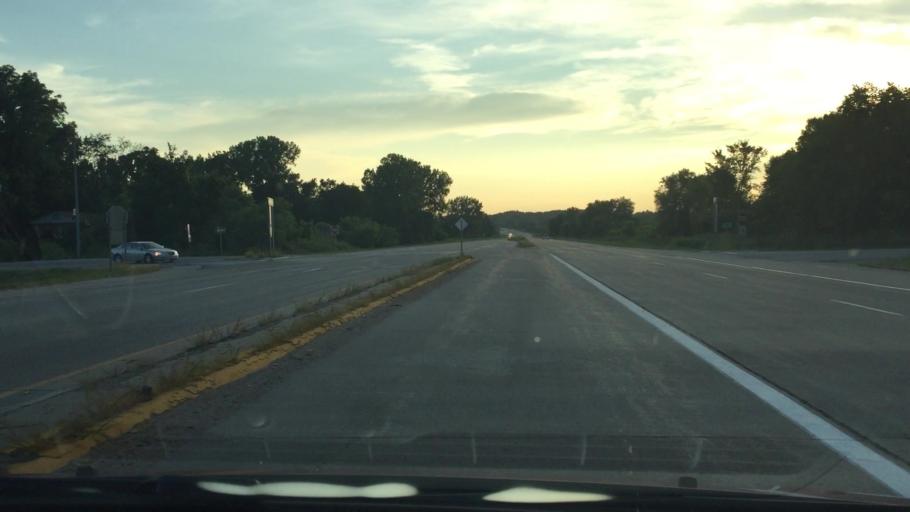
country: US
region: Iowa
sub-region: Muscatine County
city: Muscatine
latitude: 41.4529
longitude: -91.0590
